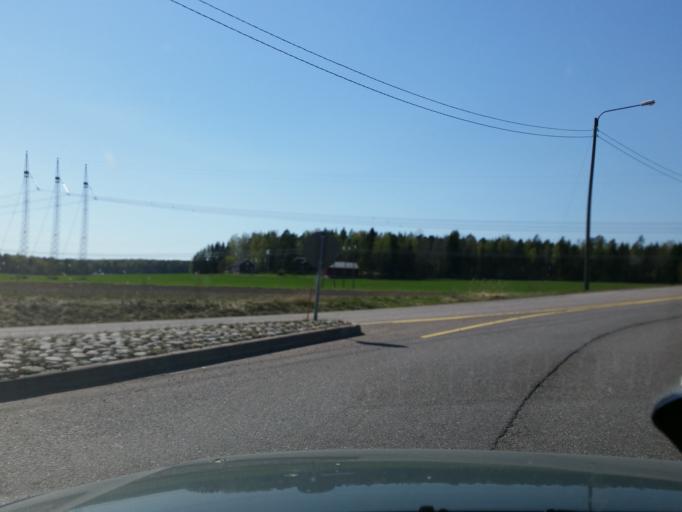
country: FI
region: Uusimaa
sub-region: Raaseporin
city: Inga
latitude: 60.0489
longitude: 23.9463
